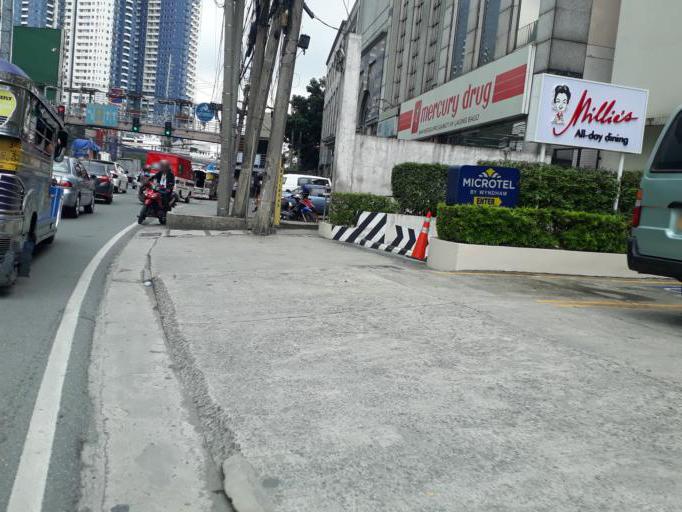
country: PH
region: Metro Manila
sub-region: Marikina
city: Calumpang
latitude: 14.6078
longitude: 121.0780
